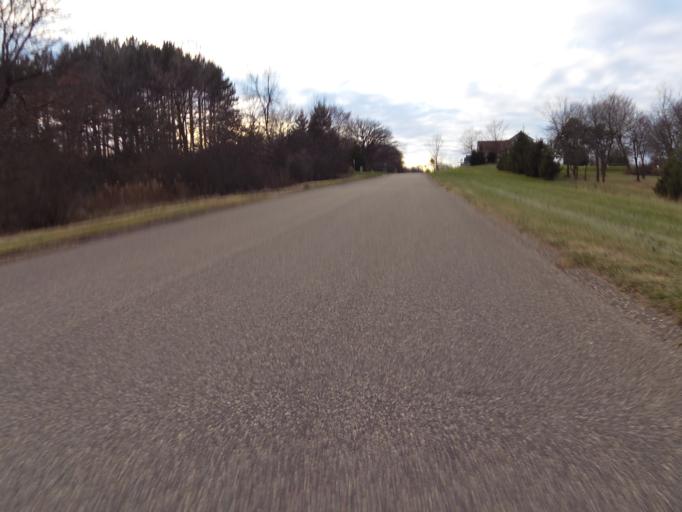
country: US
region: Minnesota
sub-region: Washington County
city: Bayport
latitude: 45.0071
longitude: -92.7961
